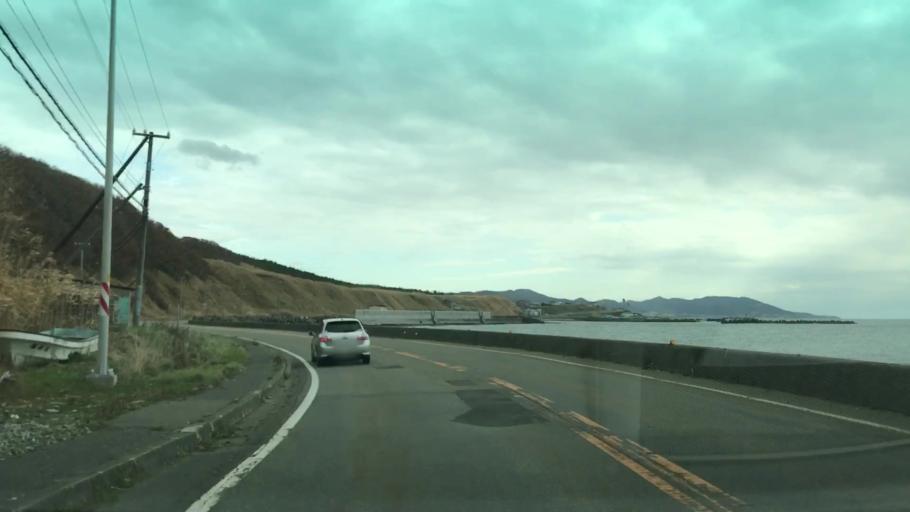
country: JP
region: Hokkaido
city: Shizunai-furukawacho
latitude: 42.0511
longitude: 143.0916
